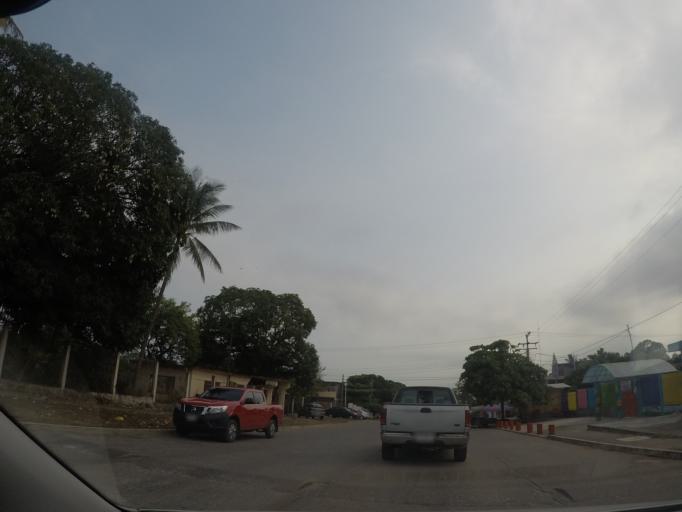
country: MX
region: Oaxaca
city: Matias Romero
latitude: 16.8728
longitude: -95.0468
